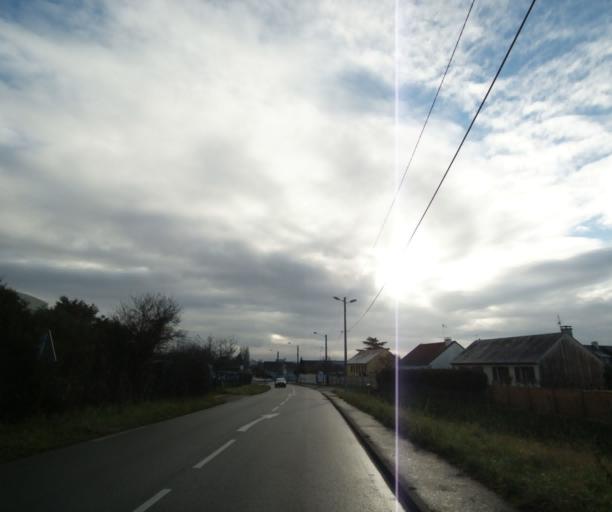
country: FR
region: Pays de la Loire
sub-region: Departement de la Sarthe
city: La Chapelle-Saint-Aubin
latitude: 48.0243
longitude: 0.1744
